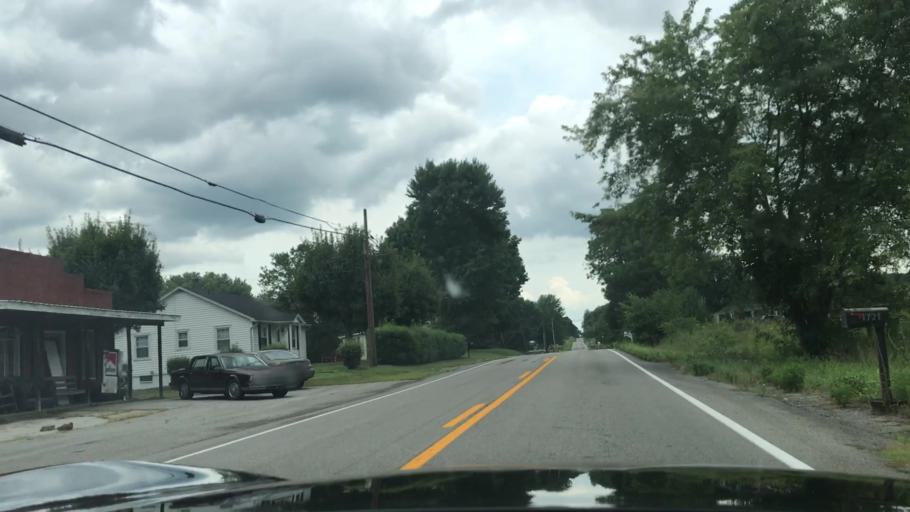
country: US
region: Kentucky
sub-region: Muhlenberg County
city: Central City
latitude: 37.2020
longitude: -87.0091
